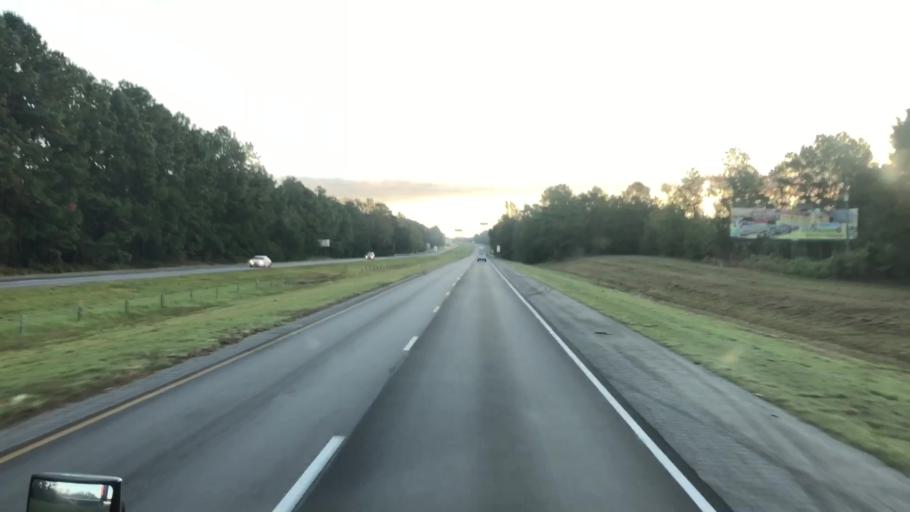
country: US
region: South Carolina
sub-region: Clarendon County
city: Manning
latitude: 33.5928
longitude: -80.3461
